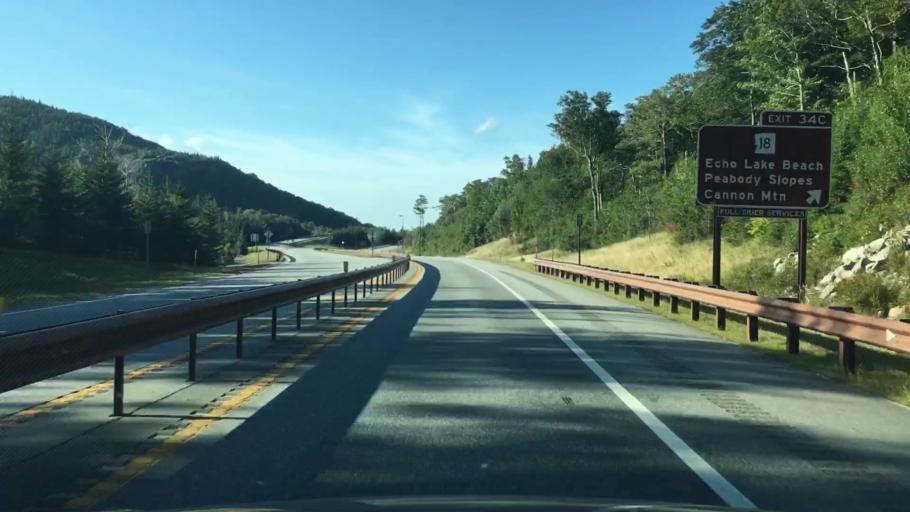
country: US
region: New Hampshire
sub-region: Grafton County
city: Deerfield
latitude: 44.1751
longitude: -71.6897
